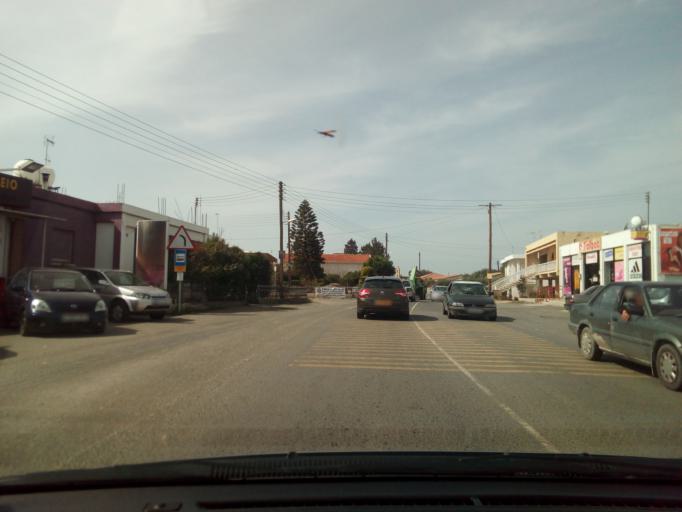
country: CY
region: Lefkosia
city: Kato Deftera
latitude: 35.0869
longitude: 33.2821
